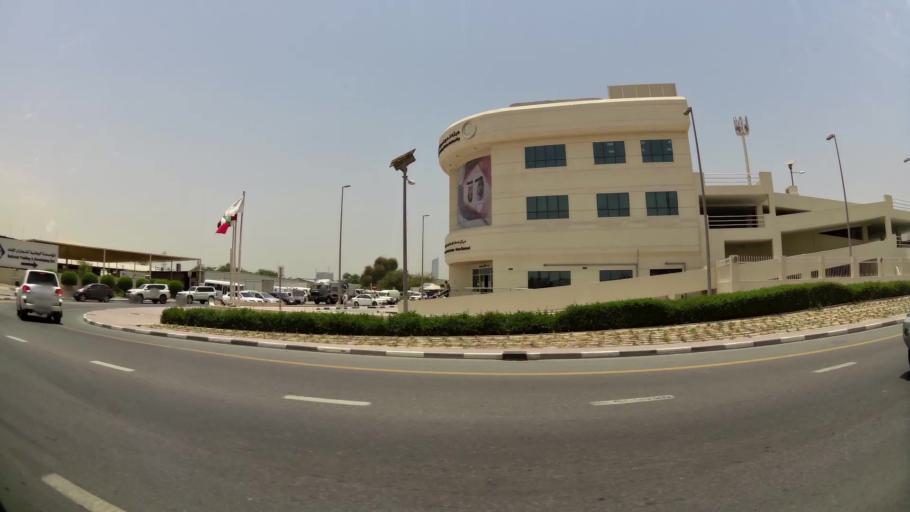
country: AE
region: Ash Shariqah
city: Sharjah
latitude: 25.2251
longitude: 55.3766
